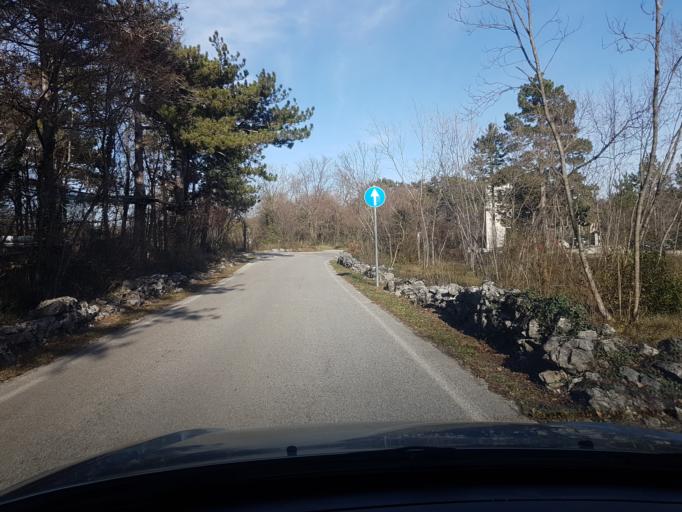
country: IT
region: Friuli Venezia Giulia
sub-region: Provincia di Trieste
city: Sistiana-Visogliano
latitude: 45.7831
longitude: 13.6401
